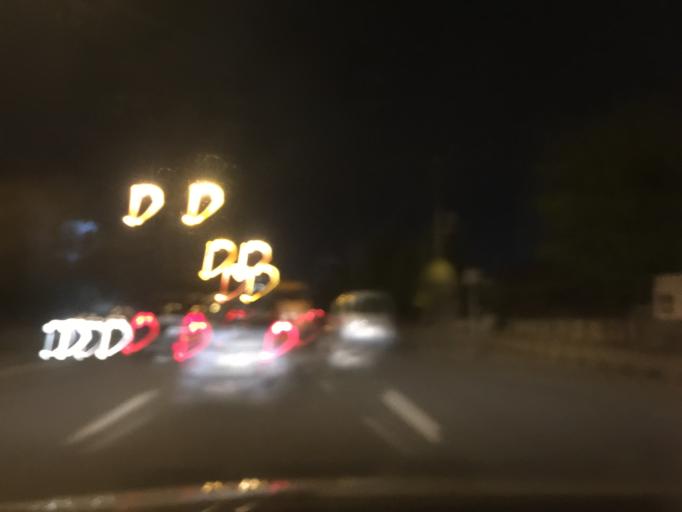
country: JO
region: Amman
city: Wadi as Sir
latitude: 31.9678
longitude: 35.8421
